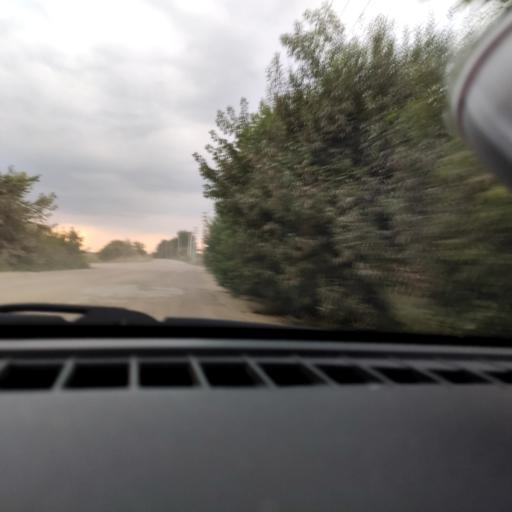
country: RU
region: Perm
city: Kondratovo
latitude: 57.9981
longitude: 56.0019
